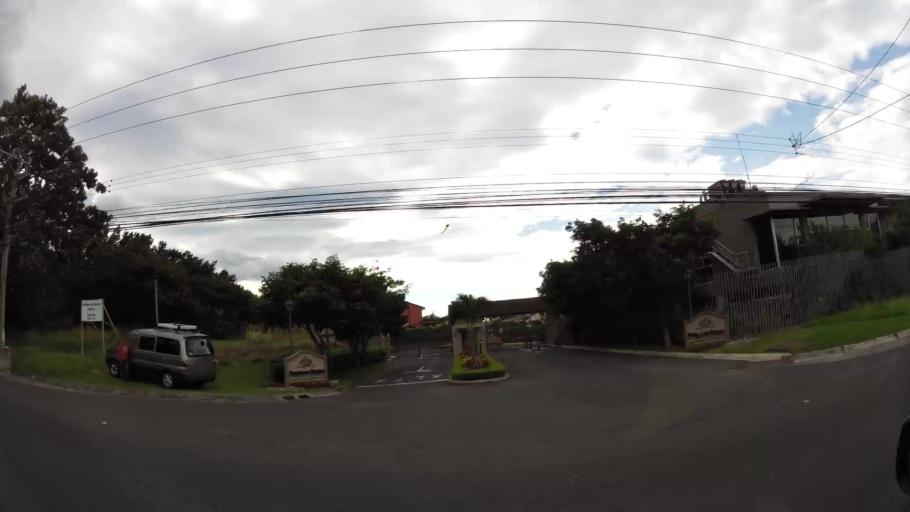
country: CR
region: San Jose
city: Santa Ana
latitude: 9.9394
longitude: -84.1890
